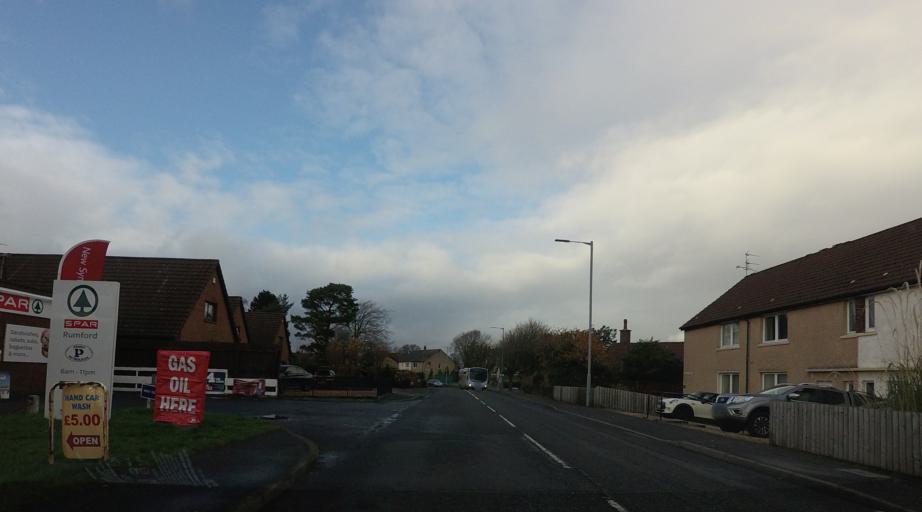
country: GB
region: Scotland
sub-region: Falkirk
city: Polmont
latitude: 55.9769
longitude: -3.7124
